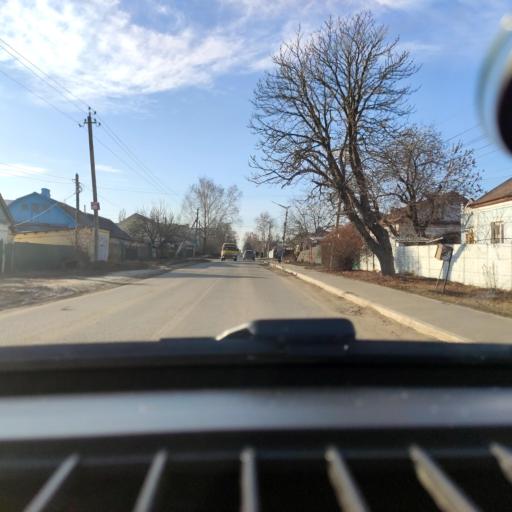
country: RU
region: Voronezj
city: Semiluki
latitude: 51.6986
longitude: 39.0250
